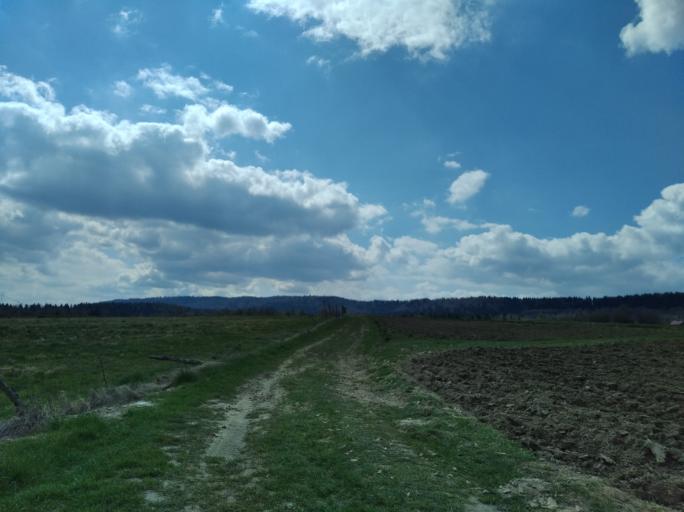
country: PL
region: Subcarpathian Voivodeship
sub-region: Powiat strzyzowski
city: Strzyzow
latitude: 49.8419
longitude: 21.7802
